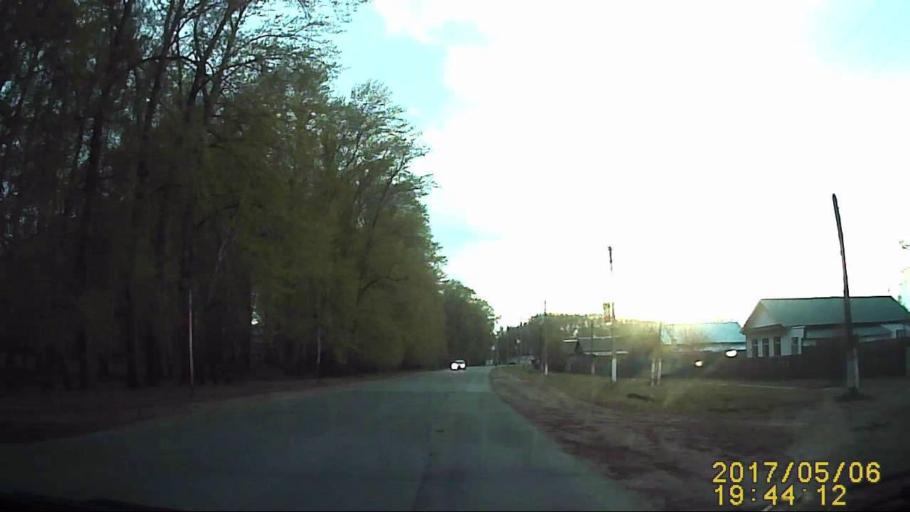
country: RU
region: Ulyanovsk
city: Staraya Mayna
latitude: 54.6076
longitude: 48.9312
